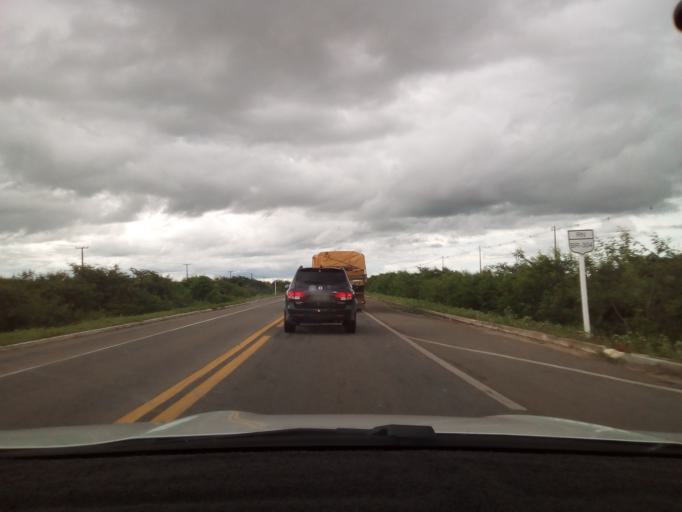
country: BR
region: Rio Grande do Norte
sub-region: Barauna
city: Barauna
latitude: -4.9200
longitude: -37.4217
